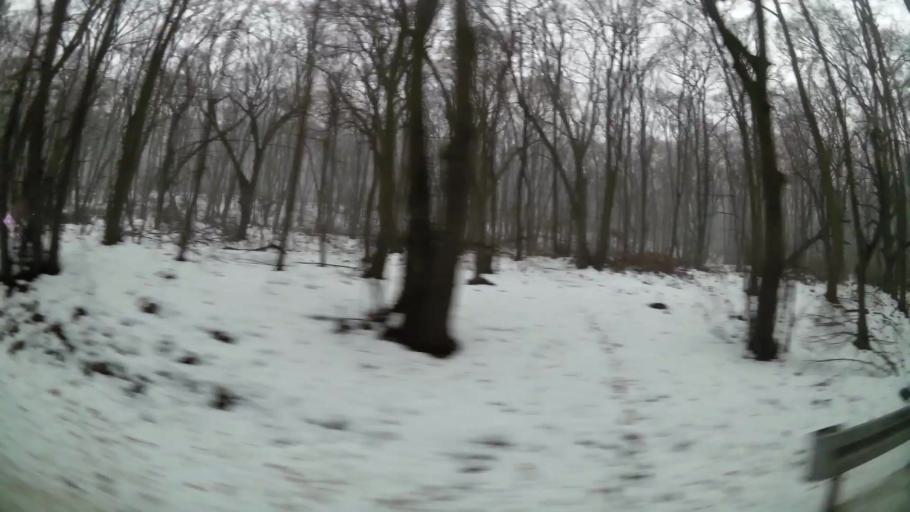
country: RS
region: Central Serbia
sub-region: Belgrade
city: Cukarica
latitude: 44.7747
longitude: 20.4304
